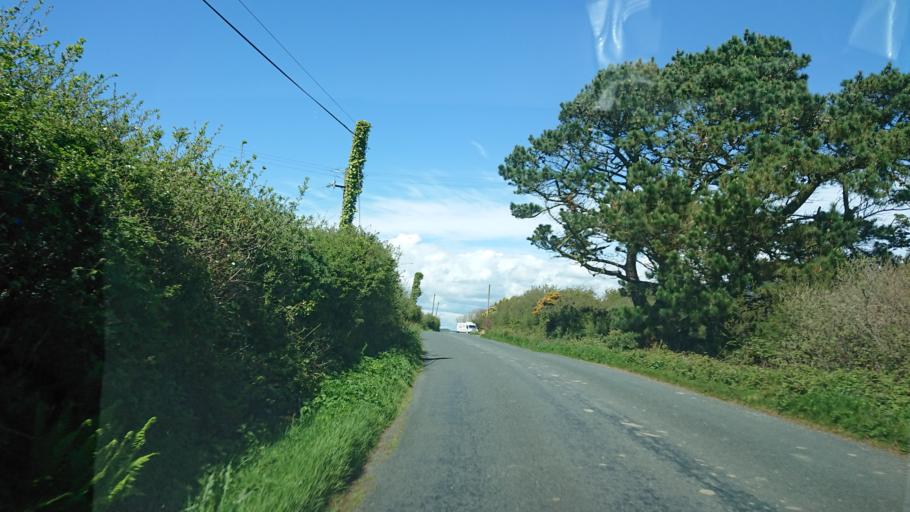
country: IE
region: Munster
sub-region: Waterford
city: Dunmore East
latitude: 52.1648
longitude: -7.0641
